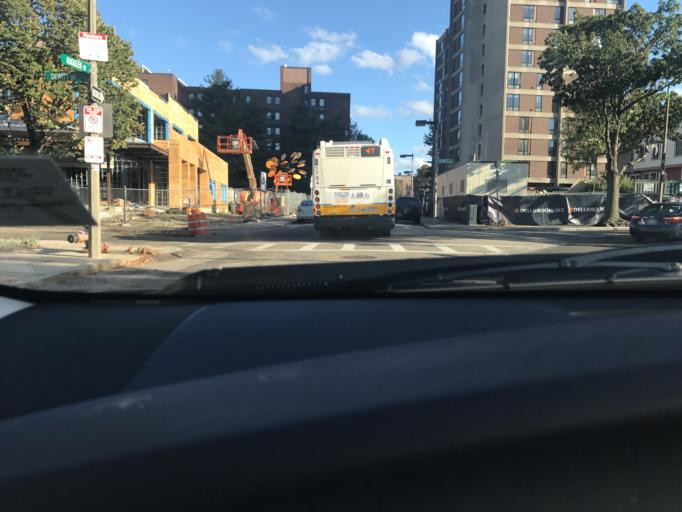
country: US
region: Massachusetts
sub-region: Suffolk County
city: South Boston
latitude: 42.3329
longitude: -71.0853
